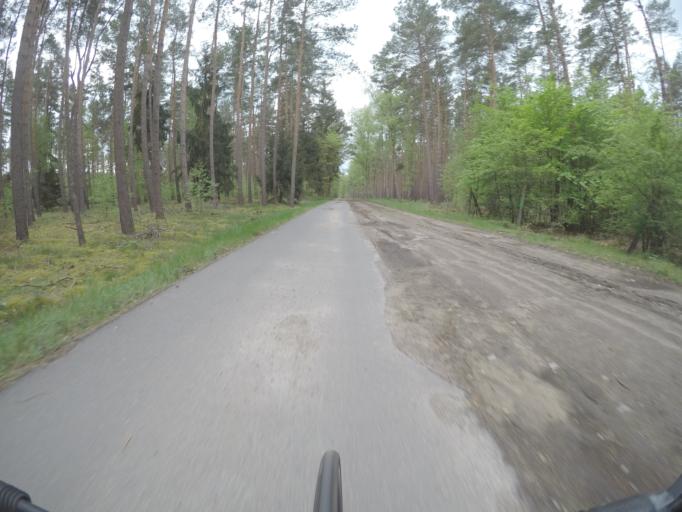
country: DE
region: Brandenburg
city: Marienwerder
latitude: 52.8192
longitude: 13.6412
